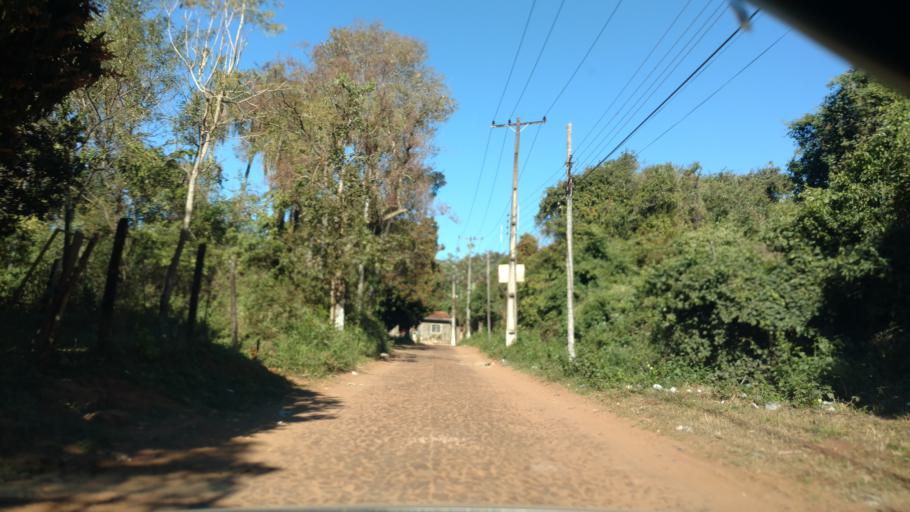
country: PY
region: Central
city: Capiata
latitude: -25.3599
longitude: -57.4173
